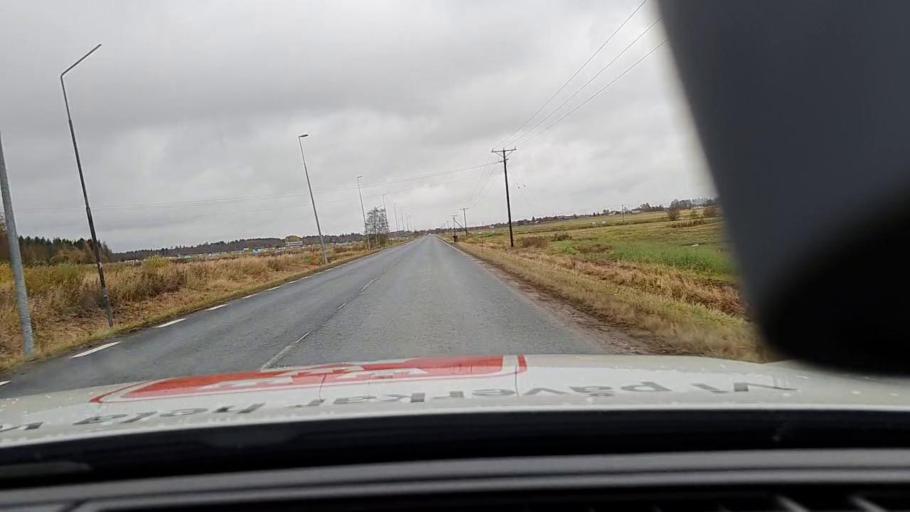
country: FI
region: Lapland
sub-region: Kemi-Tornio
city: Tornio
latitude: 65.9789
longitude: 24.0279
